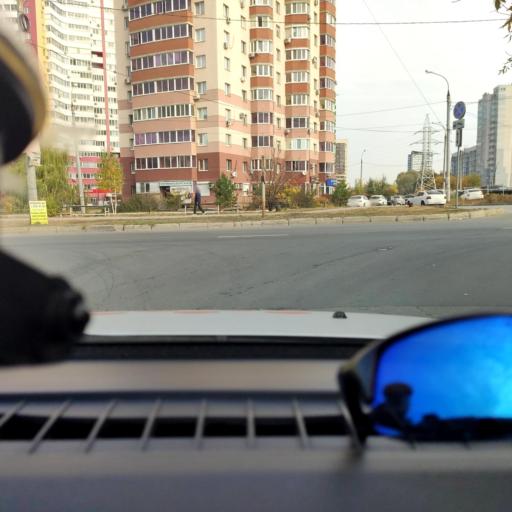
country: RU
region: Samara
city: Samara
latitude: 53.2395
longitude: 50.1863
